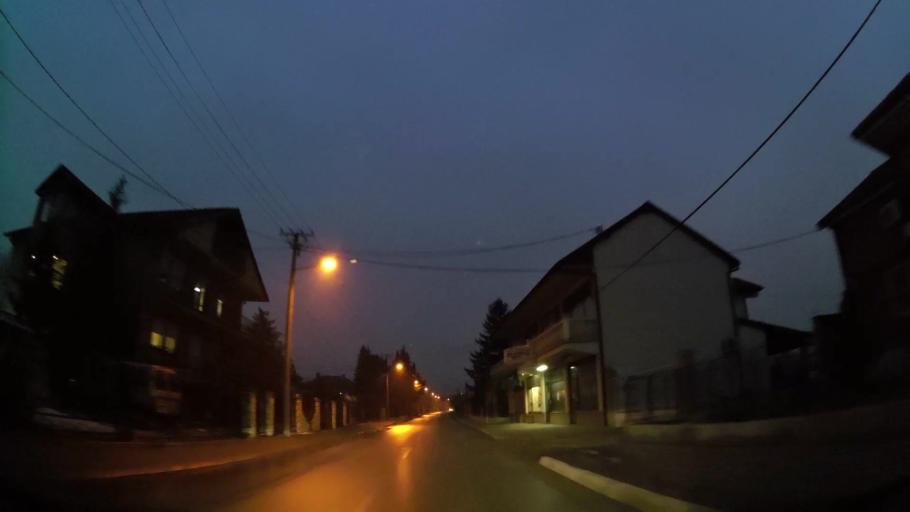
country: MK
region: Kisela Voda
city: Kisela Voda
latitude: 41.9705
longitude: 21.4843
